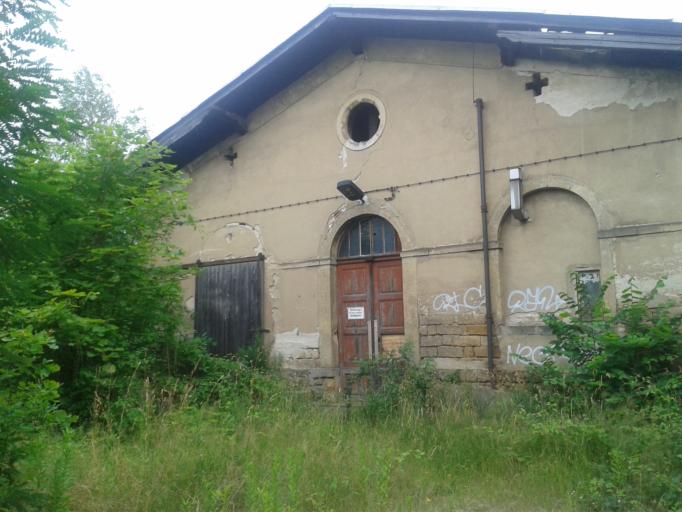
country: DE
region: Saxony
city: Dresden
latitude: 51.0668
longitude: 13.7355
